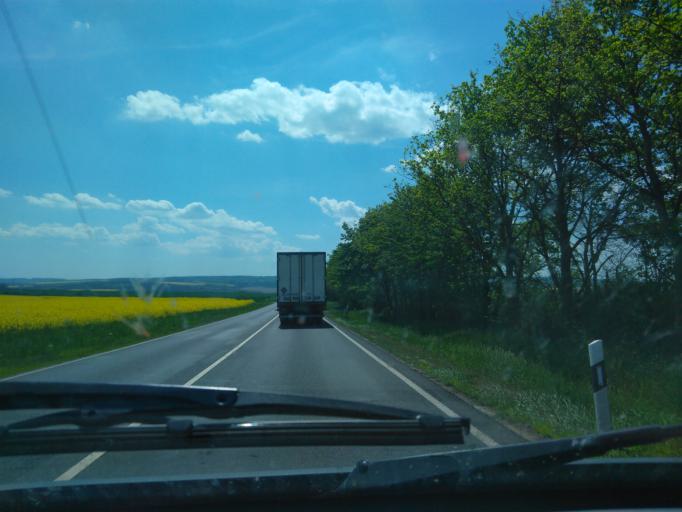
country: DE
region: Thuringia
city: Umpferstedt
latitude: 50.9598
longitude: 11.4072
